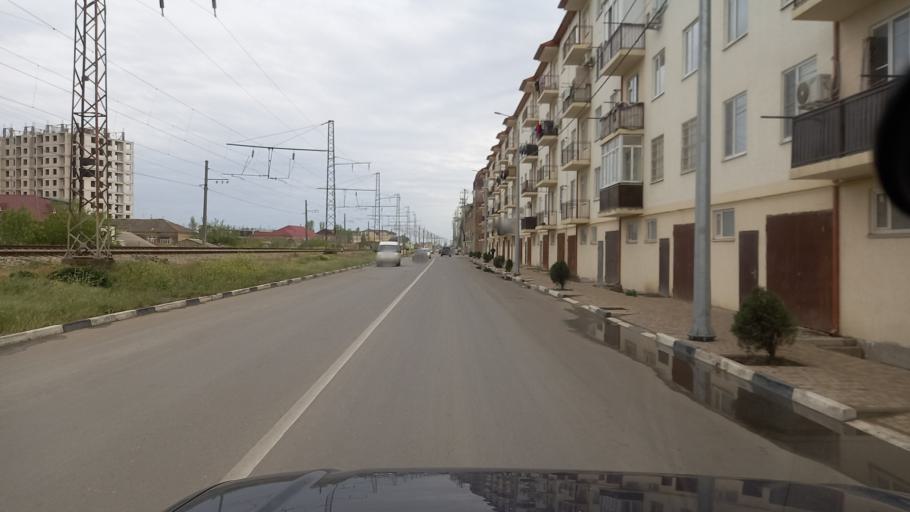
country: RU
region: Dagestan
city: Derbent
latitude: 42.0708
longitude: 48.2987
